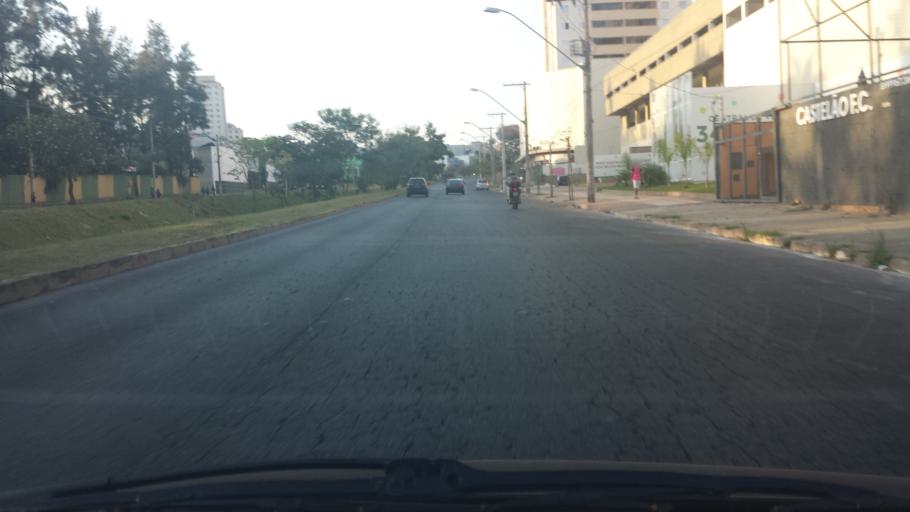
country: BR
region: Minas Gerais
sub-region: Belo Horizonte
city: Belo Horizonte
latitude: -19.8877
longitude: -43.9940
